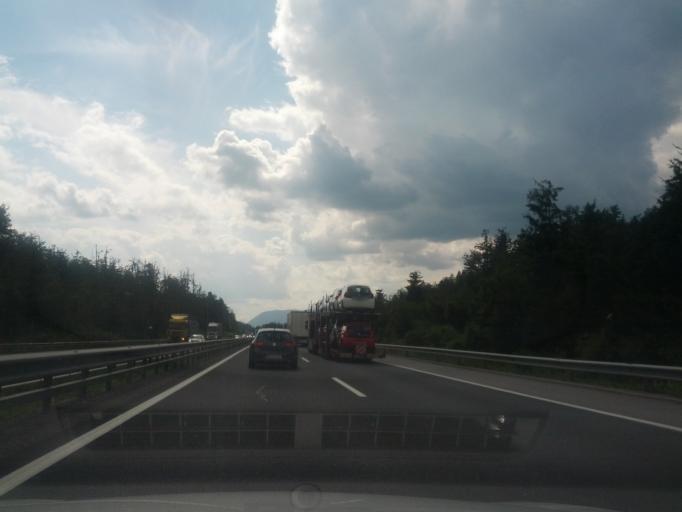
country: SI
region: Postojna
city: Postojna
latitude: 45.7983
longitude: 14.2519
